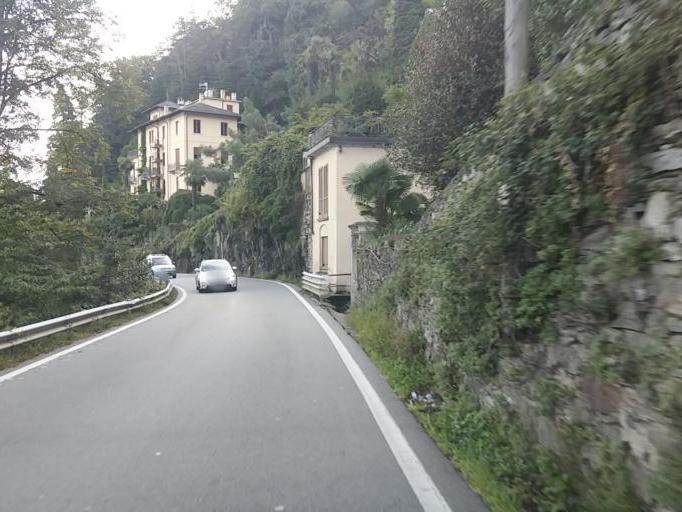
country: IT
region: Piedmont
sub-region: Provincia Verbano-Cusio-Ossola
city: Cannobio
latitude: 46.0568
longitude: 8.7039
